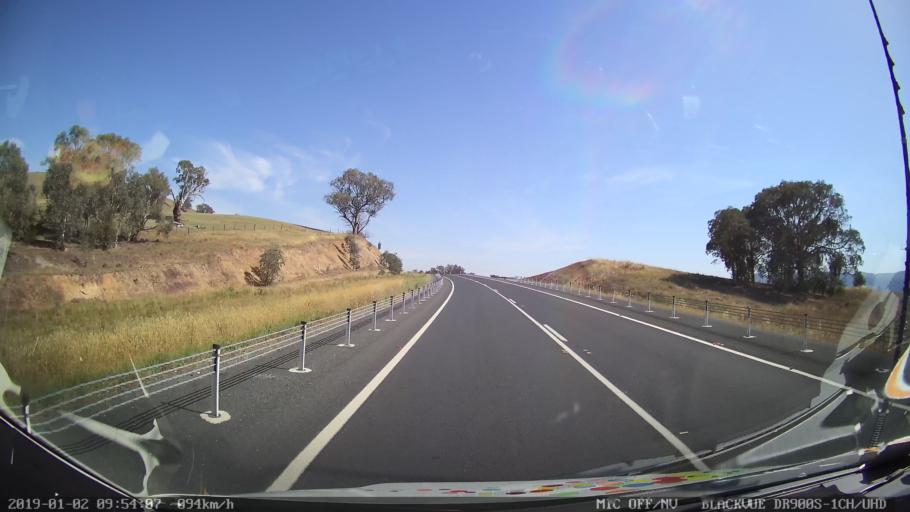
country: AU
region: New South Wales
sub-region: Tumut Shire
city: Tumut
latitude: -35.2393
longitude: 148.1980
